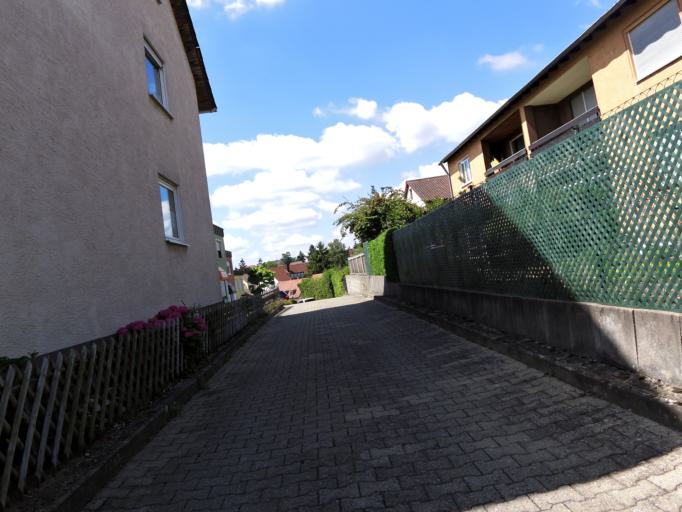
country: DE
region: Bavaria
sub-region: Regierungsbezirk Unterfranken
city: Gerbrunn
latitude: 49.7808
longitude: 9.9833
